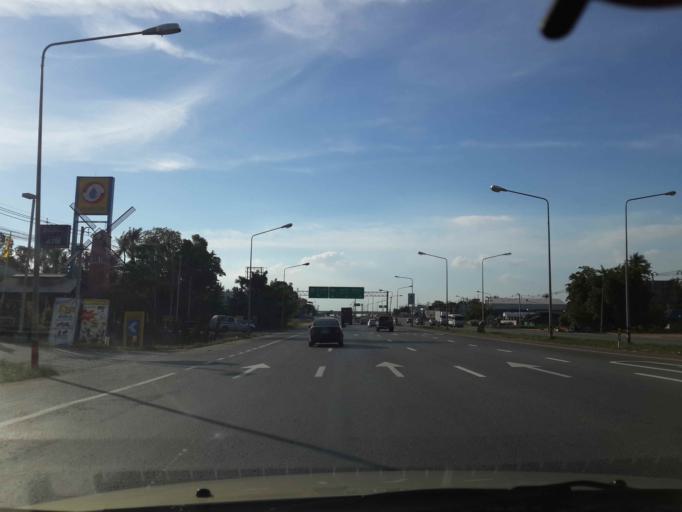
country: TH
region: Chon Buri
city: Phatthaya
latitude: 12.9470
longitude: 100.9914
